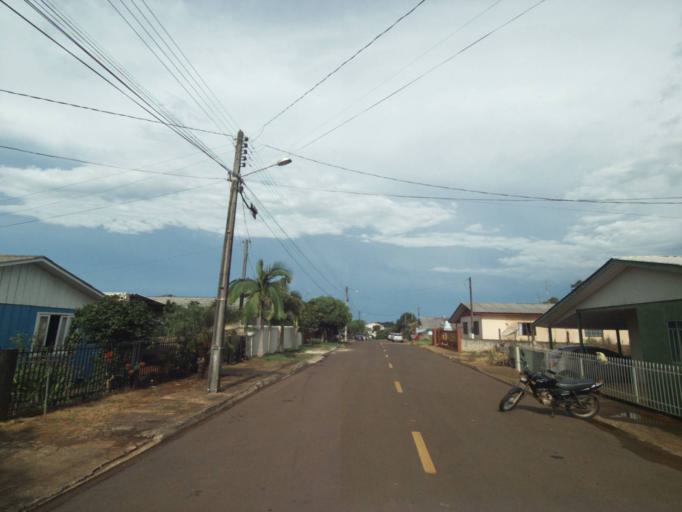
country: BR
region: Parana
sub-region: Guaraniacu
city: Guaraniacu
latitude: -25.1042
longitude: -52.8667
